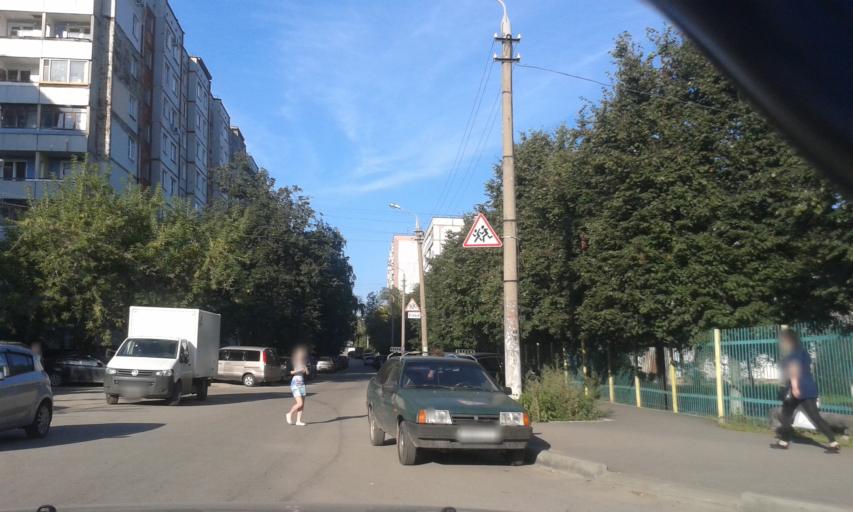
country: RU
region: Tula
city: Tula
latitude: 54.1947
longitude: 37.5959
